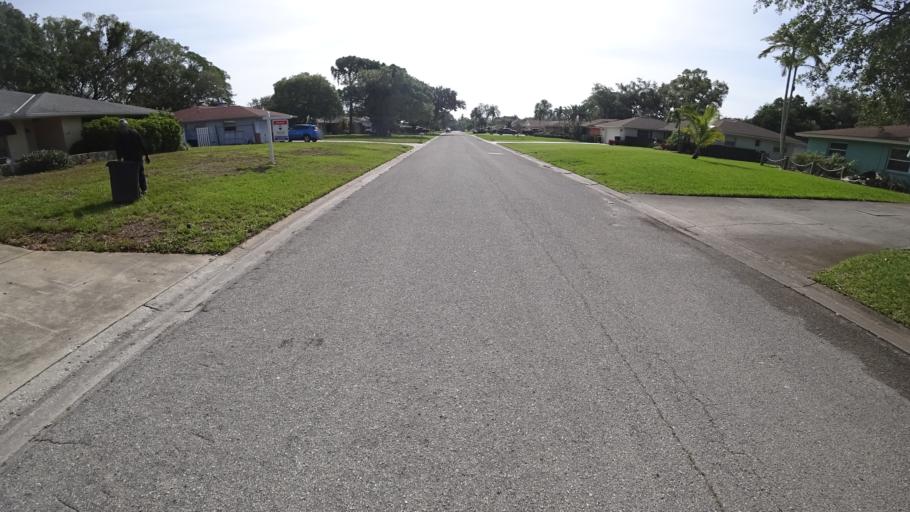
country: US
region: Florida
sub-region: Manatee County
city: West Bradenton
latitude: 27.5134
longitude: -82.6392
